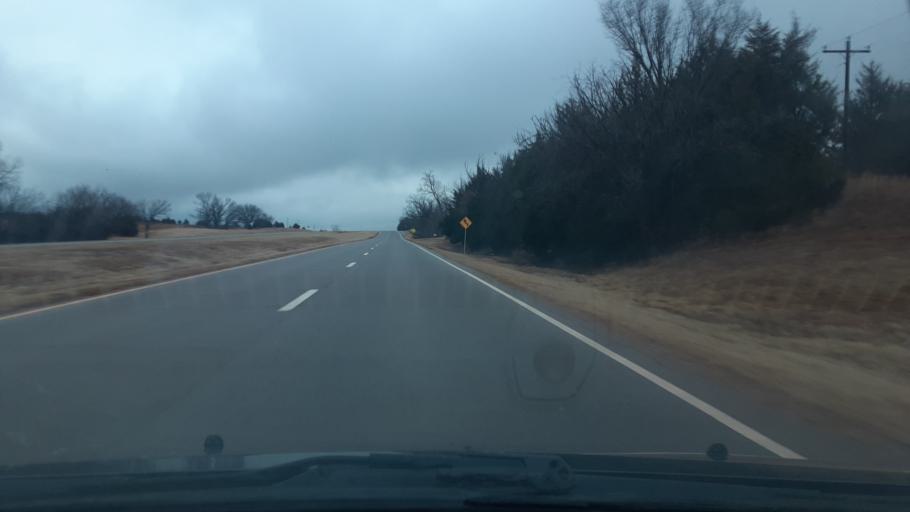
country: US
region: Oklahoma
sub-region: Payne County
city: Stillwater
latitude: 36.1158
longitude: -97.1537
